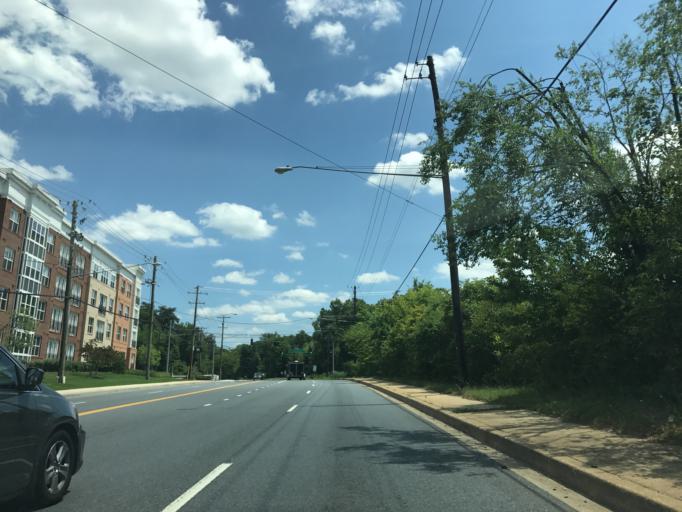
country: US
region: Maryland
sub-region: Prince George's County
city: South Laurel
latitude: 39.0606
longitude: -76.8824
